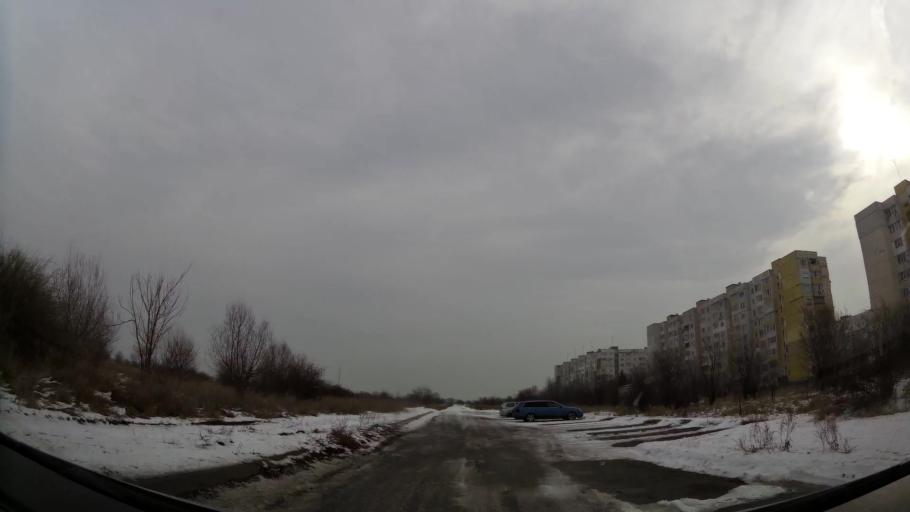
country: BG
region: Sofia-Capital
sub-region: Stolichna Obshtina
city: Sofia
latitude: 42.7148
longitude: 23.3851
